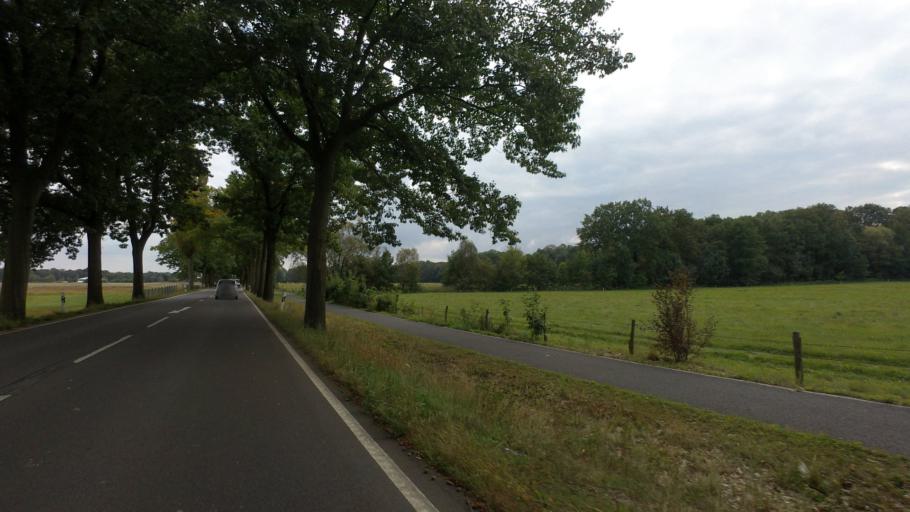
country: DE
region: Saxony
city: Konigswartha
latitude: 51.3596
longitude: 14.3167
